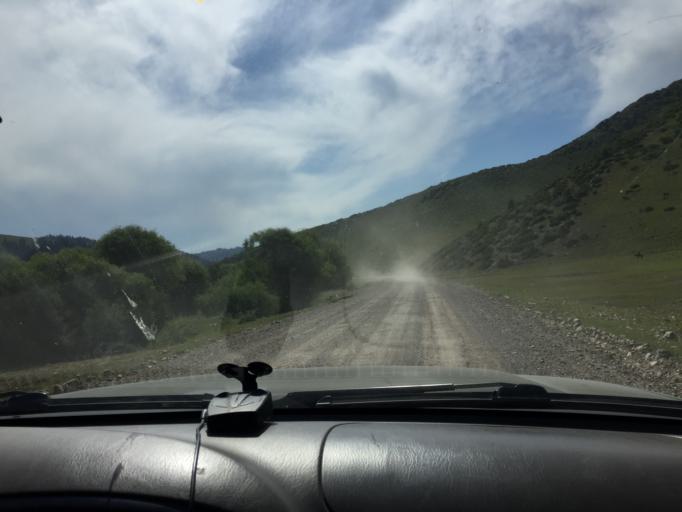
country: KZ
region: Almaty Oblysy
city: Kegen
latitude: 42.7410
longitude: 78.9463
